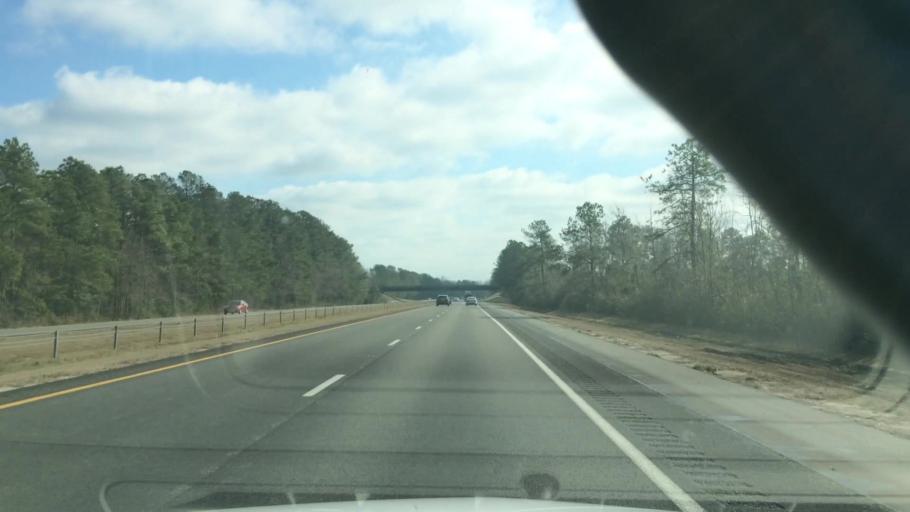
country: US
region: North Carolina
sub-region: Pender County
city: Burgaw
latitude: 34.6149
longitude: -77.9237
